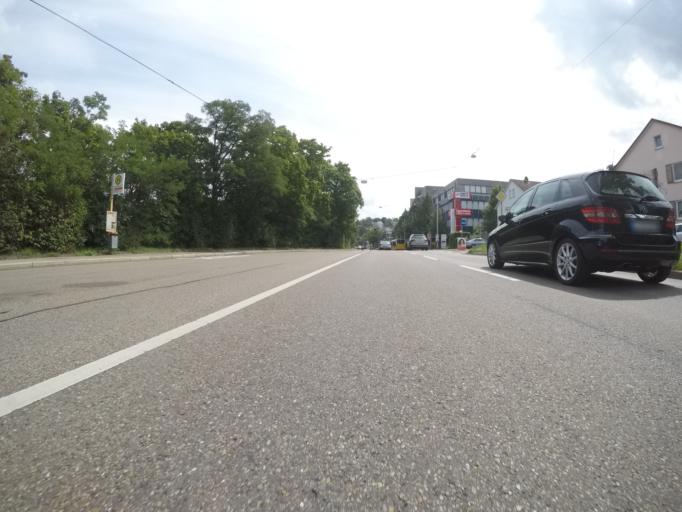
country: DE
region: Baden-Wuerttemberg
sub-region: Regierungsbezirk Stuttgart
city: Stuttgart
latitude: 48.7695
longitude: 9.1448
